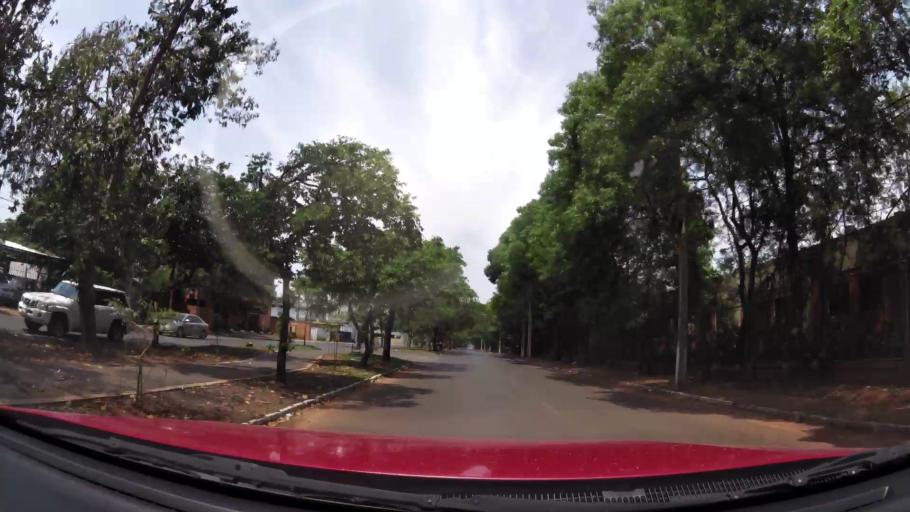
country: PY
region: Central
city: Fernando de la Mora
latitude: -25.3097
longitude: -57.5653
